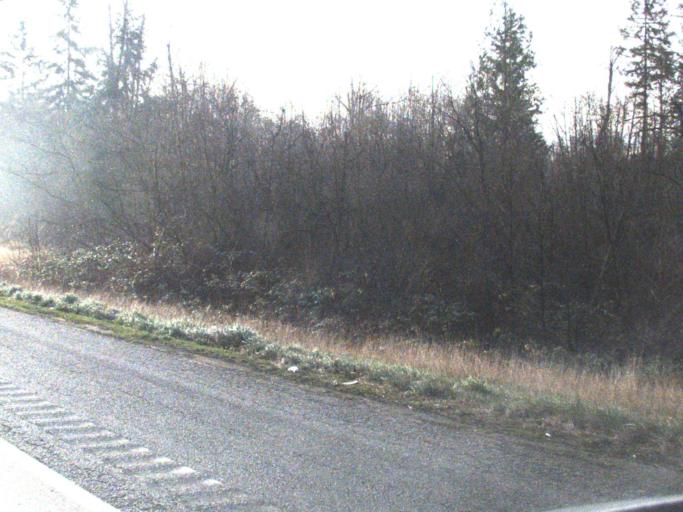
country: US
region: Washington
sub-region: Snohomish County
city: Bryant
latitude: 48.2435
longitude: -122.2461
